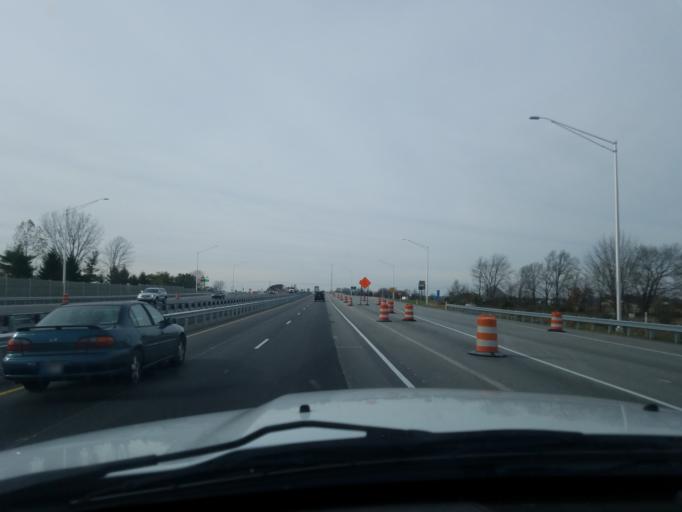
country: US
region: Indiana
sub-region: Madison County
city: Ingalls
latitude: 39.9931
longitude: -85.8372
